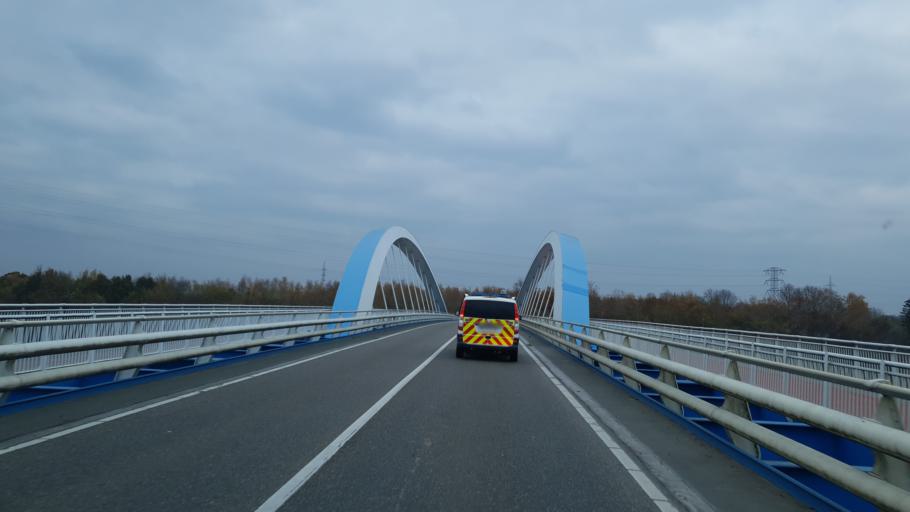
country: BE
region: Flanders
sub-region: Provincie Limburg
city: Lanaken
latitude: 50.8795
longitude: 5.6294
